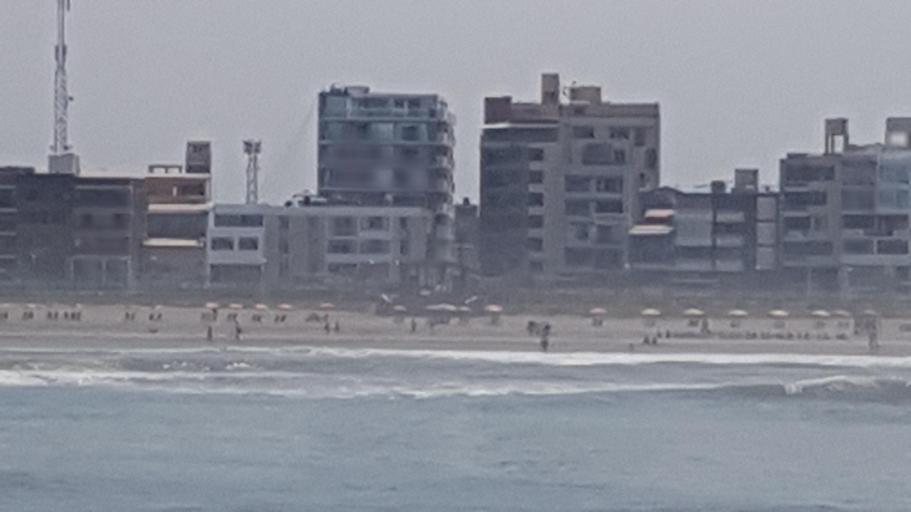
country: PE
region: Lambayeque
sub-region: Provincia de Chiclayo
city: Pimentel
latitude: -6.8394
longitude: -79.9422
